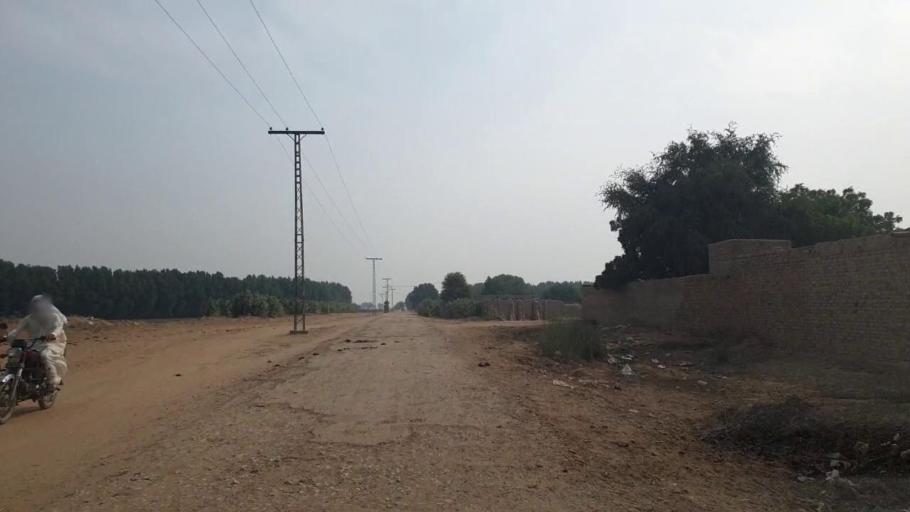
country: PK
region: Sindh
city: Sann
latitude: 26.0303
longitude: 68.1373
